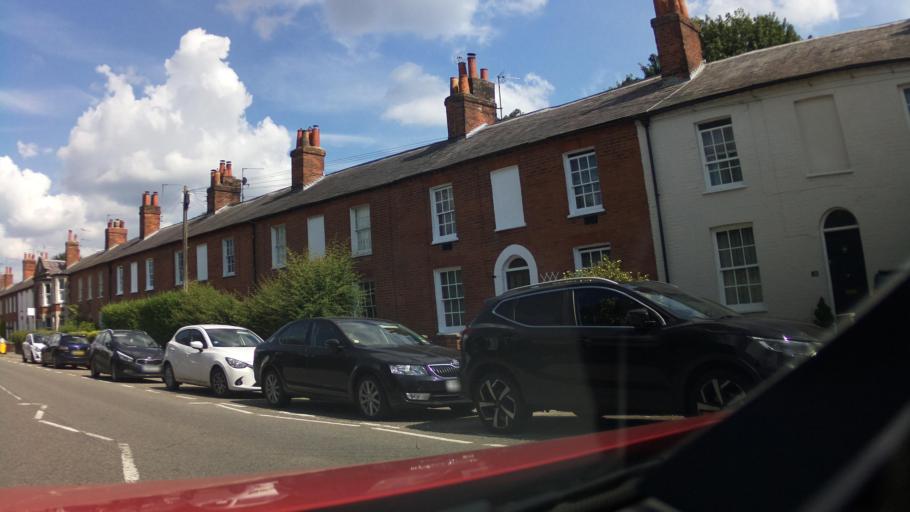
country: GB
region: England
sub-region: West Berkshire
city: Newbury
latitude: 51.4071
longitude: -1.3165
